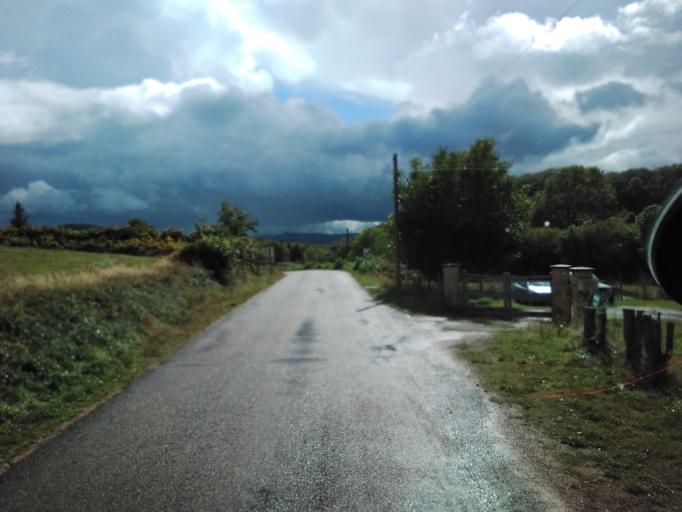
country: FR
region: Bourgogne
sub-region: Departement de la Nievre
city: Lormes
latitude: 47.3026
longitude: 3.9034
